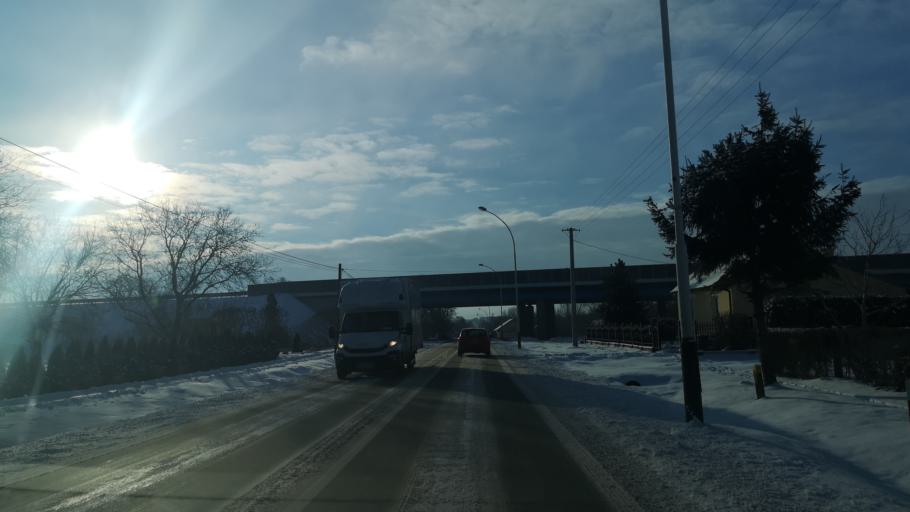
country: PL
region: Subcarpathian Voivodeship
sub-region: Powiat przeworski
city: Gorliczyna
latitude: 50.0829
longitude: 22.4930
